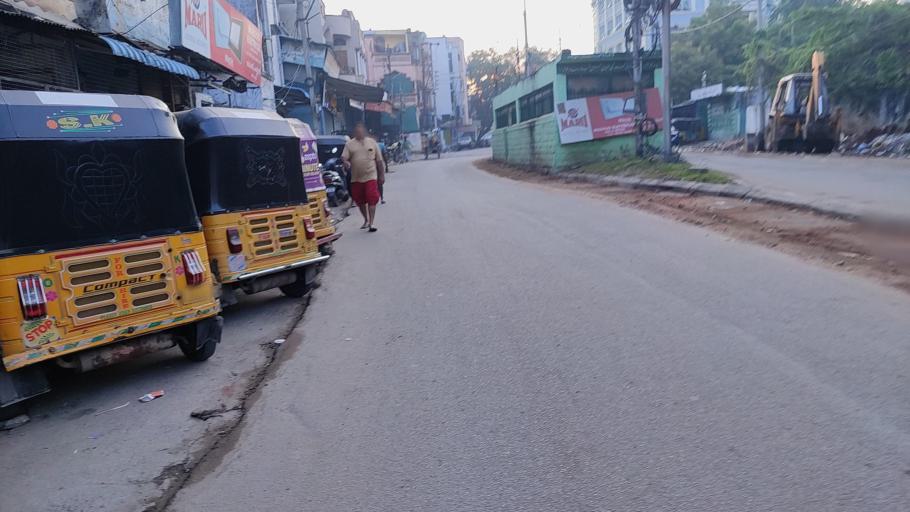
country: IN
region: Telangana
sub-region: Rangareddi
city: Gaddi Annaram
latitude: 17.3665
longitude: 78.4944
